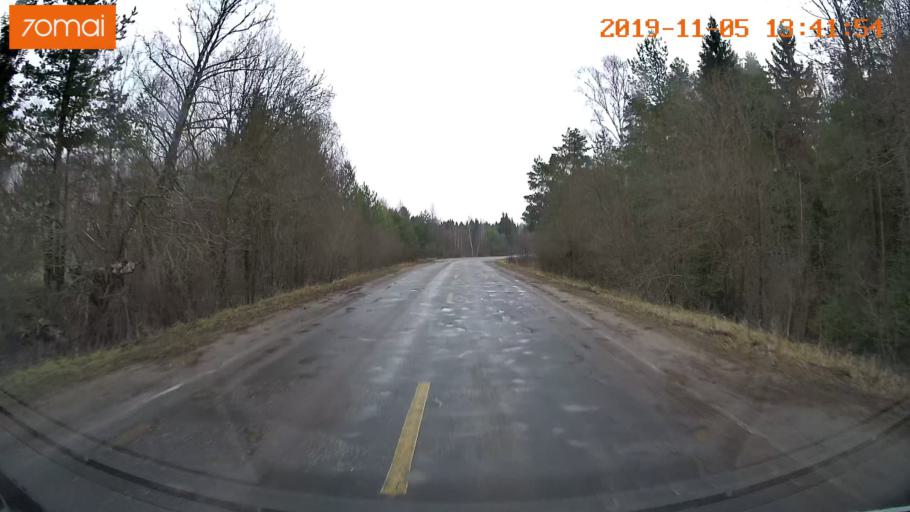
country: RU
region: Ivanovo
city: Shuya
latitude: 56.9629
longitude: 41.3881
